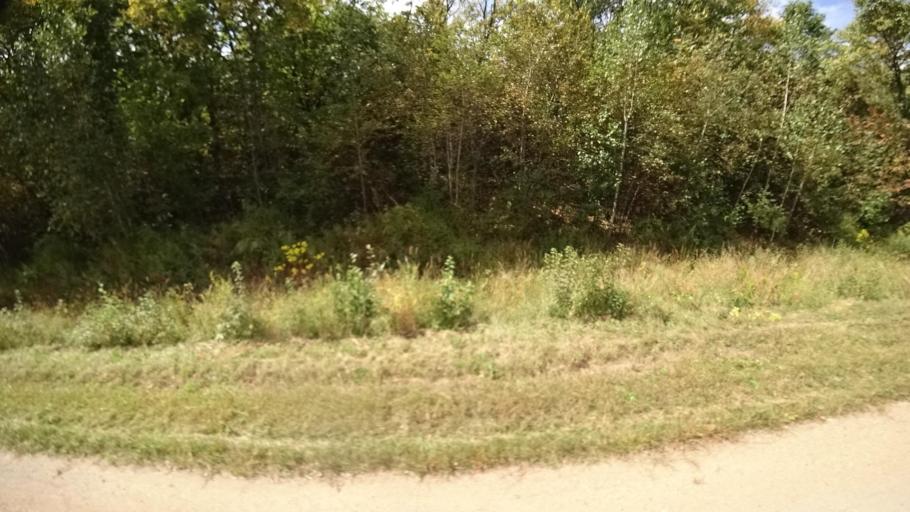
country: RU
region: Primorskiy
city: Yakovlevka
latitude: 44.6526
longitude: 133.5972
